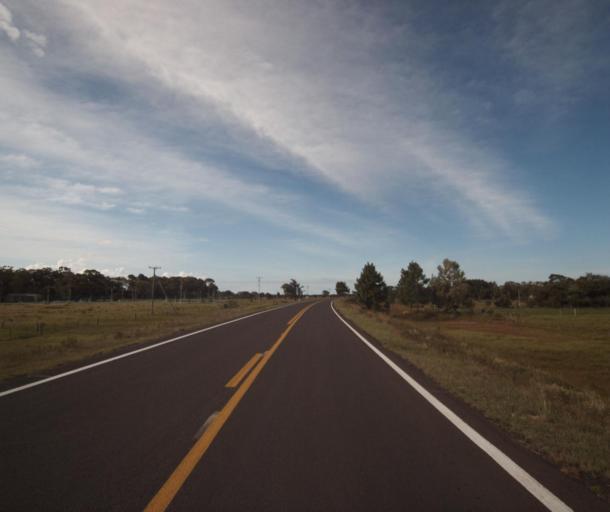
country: BR
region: Rio Grande do Sul
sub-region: Tapes
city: Tapes
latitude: -31.3224
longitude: -51.1241
